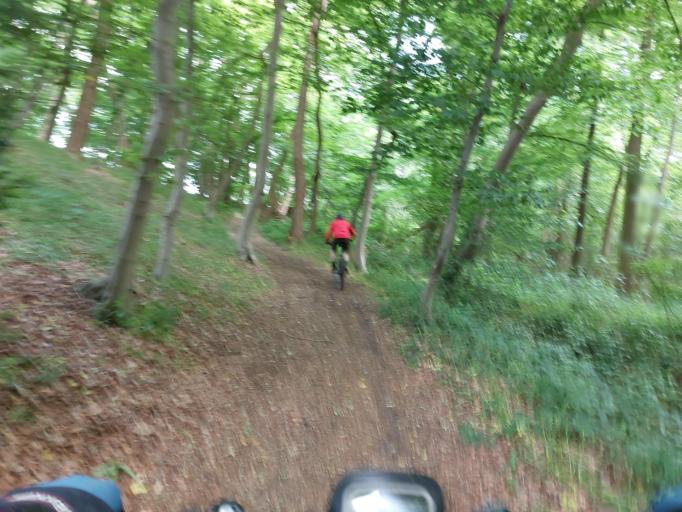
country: BE
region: Wallonia
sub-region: Province du Hainaut
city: Boussu
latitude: 50.4938
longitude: 3.7704
